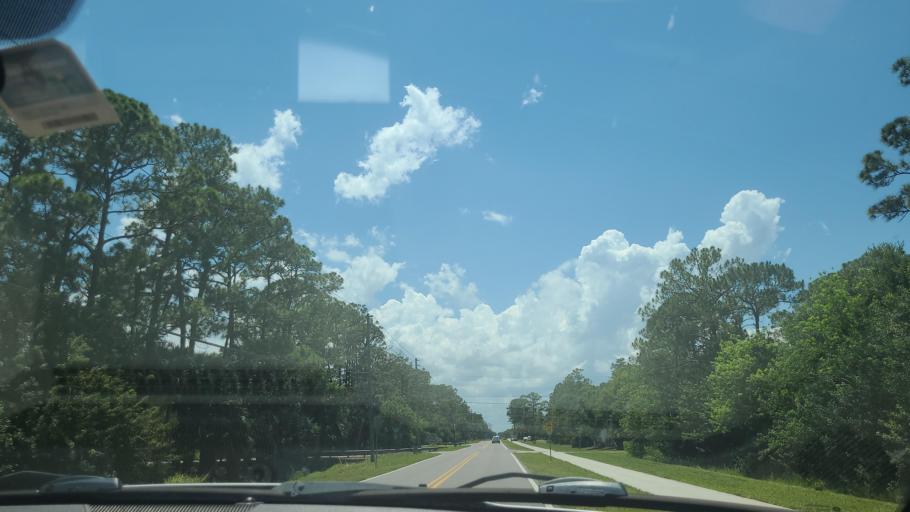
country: US
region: Florida
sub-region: Brevard County
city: Grant-Valkaria
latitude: 27.9537
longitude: -80.5830
